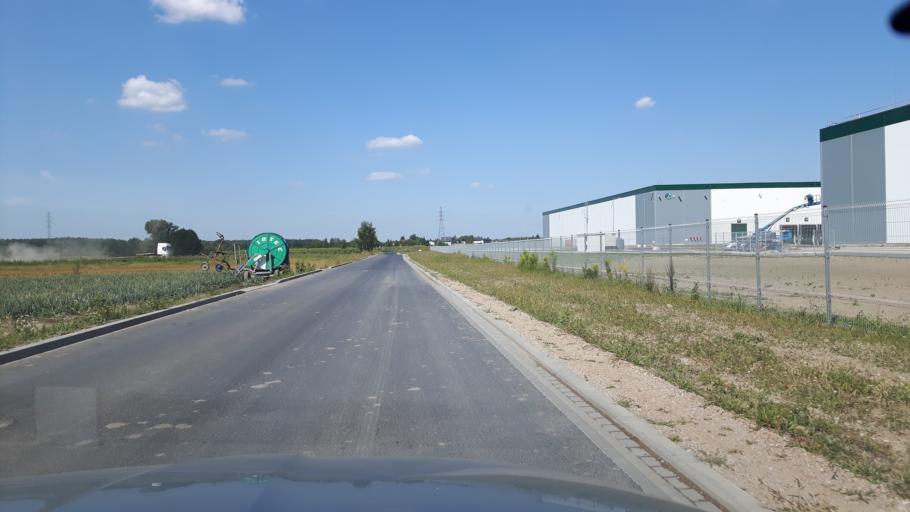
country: PL
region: Masovian Voivodeship
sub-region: Powiat pruszkowski
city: Michalowice
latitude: 52.1314
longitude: 20.8660
